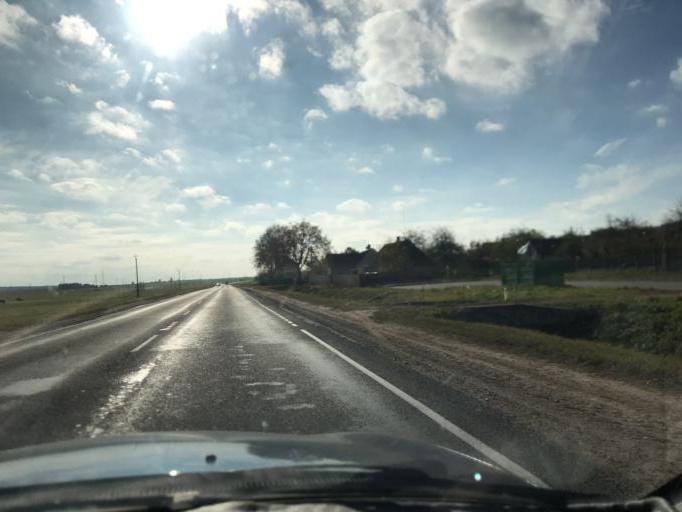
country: BY
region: Grodnenskaya
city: Voranava
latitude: 54.1543
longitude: 25.3259
